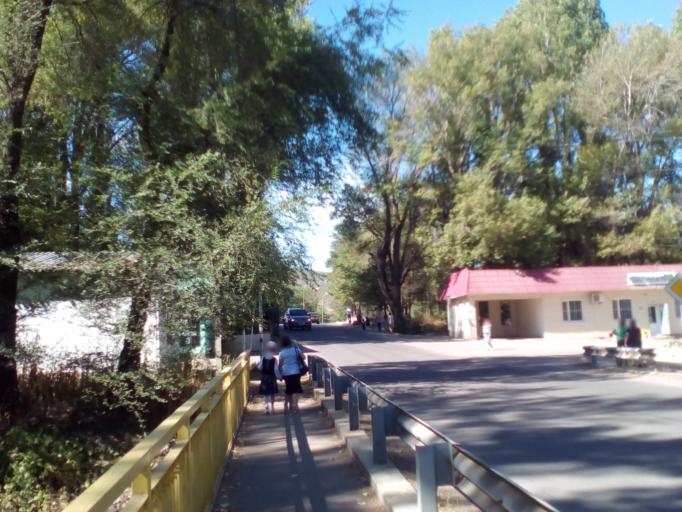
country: KZ
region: Almaty Oblysy
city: Burunday
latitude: 43.1569
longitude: 76.4179
